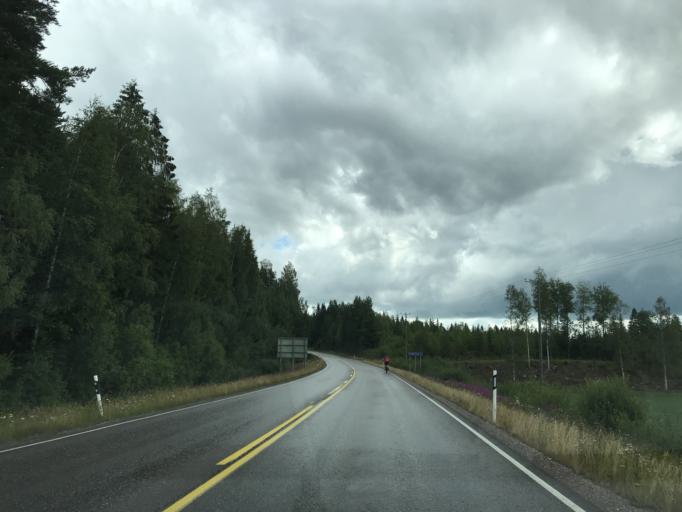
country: FI
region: Uusimaa
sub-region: Porvoo
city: Pukkila
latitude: 60.7696
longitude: 25.4780
